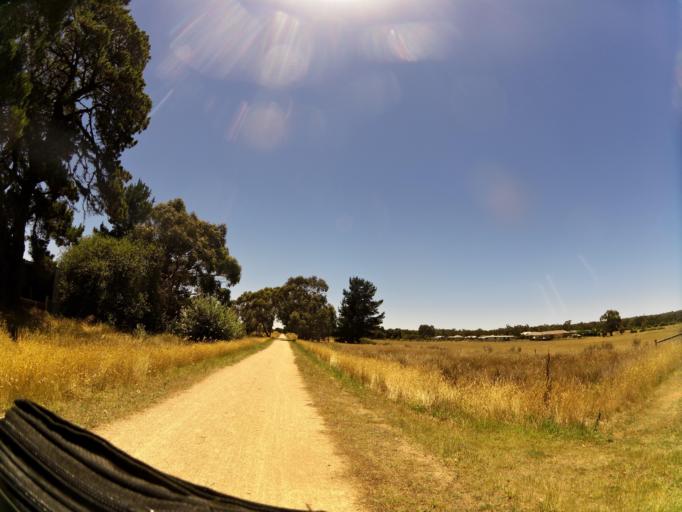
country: AU
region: Victoria
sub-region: Ballarat North
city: Delacombe
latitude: -37.5971
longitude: 143.7192
